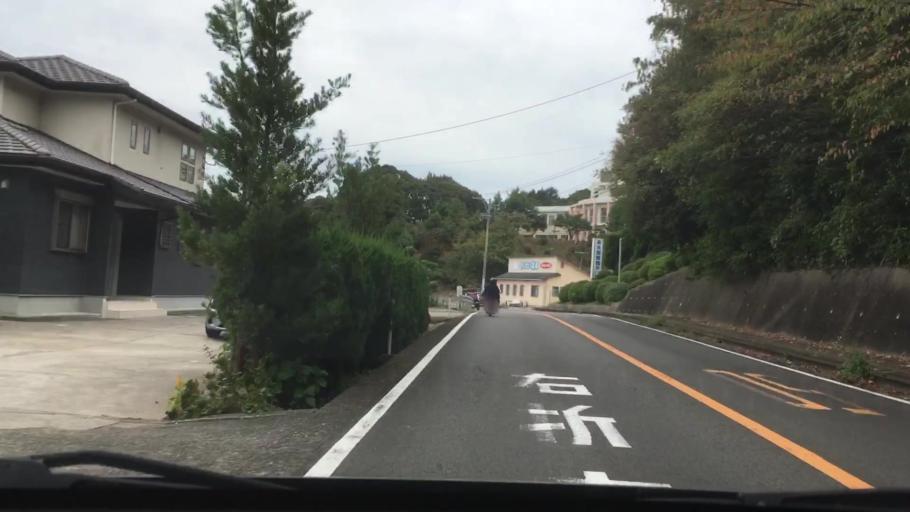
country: JP
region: Nagasaki
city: Sasebo
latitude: 33.0156
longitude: 129.7330
